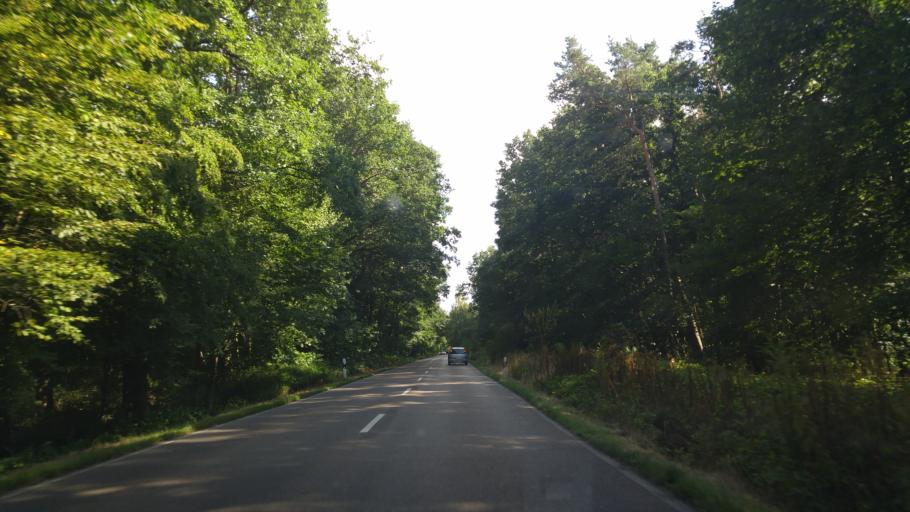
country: DE
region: Saxony-Anhalt
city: Lieskau
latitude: 51.4982
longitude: 11.8909
